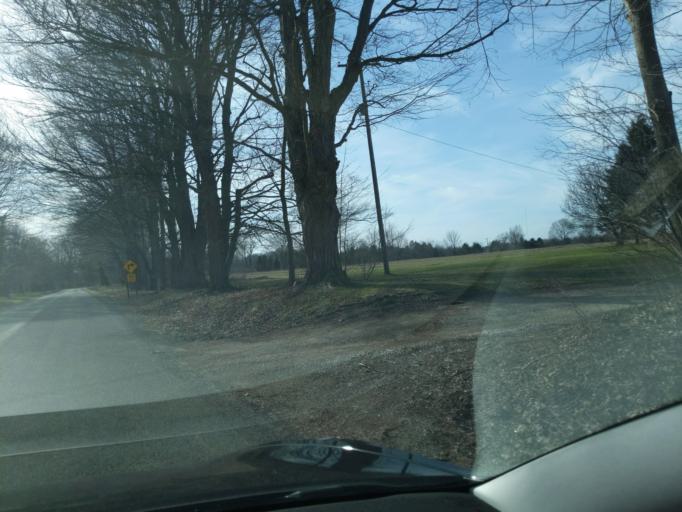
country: US
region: Michigan
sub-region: Ingham County
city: Okemos
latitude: 42.6764
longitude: -84.3806
